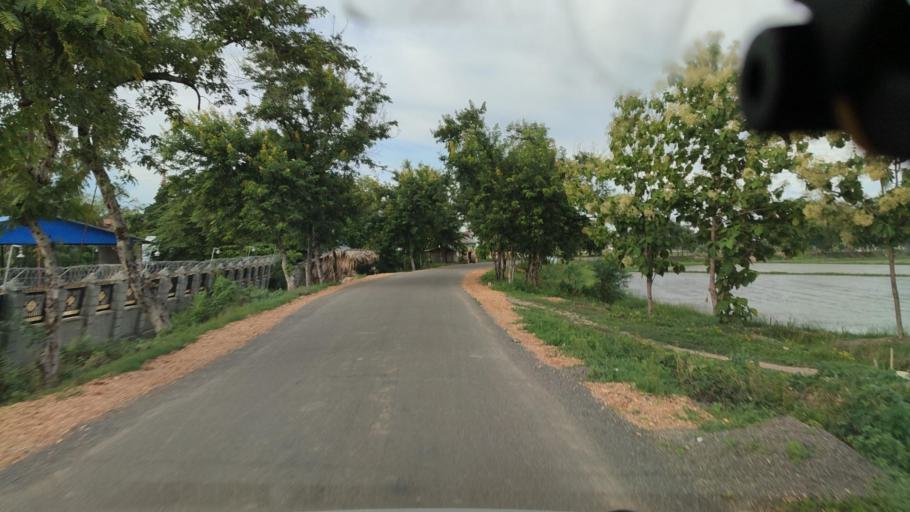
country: MM
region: Magway
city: Minbu
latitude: 20.3095
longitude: 94.7526
